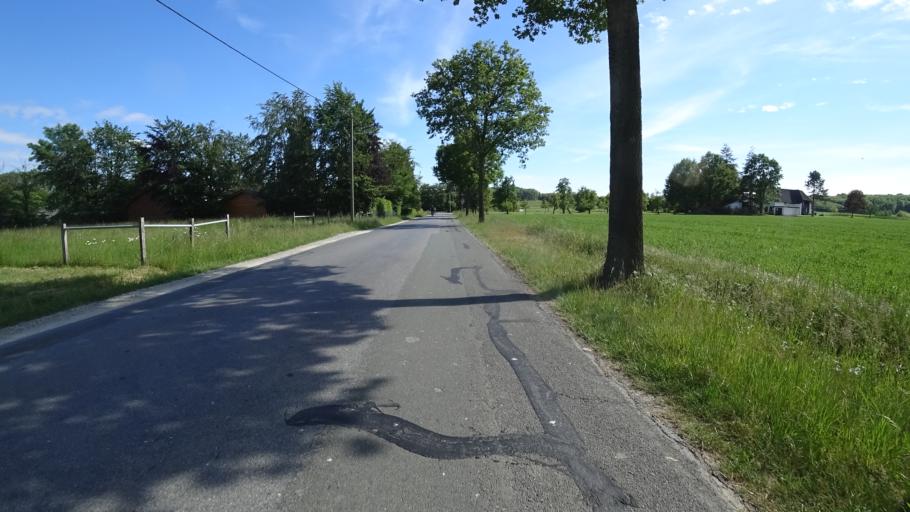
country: DE
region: North Rhine-Westphalia
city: Oelde
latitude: 51.8151
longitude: 8.2223
